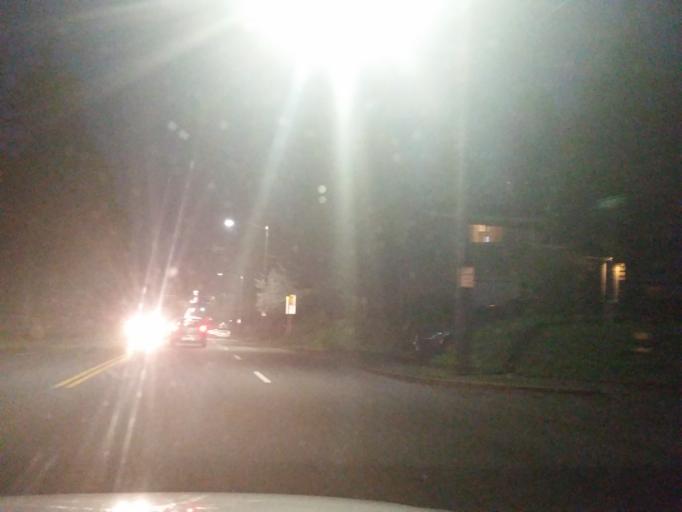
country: US
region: Washington
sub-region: King County
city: Shoreline
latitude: 47.7342
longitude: -122.3318
